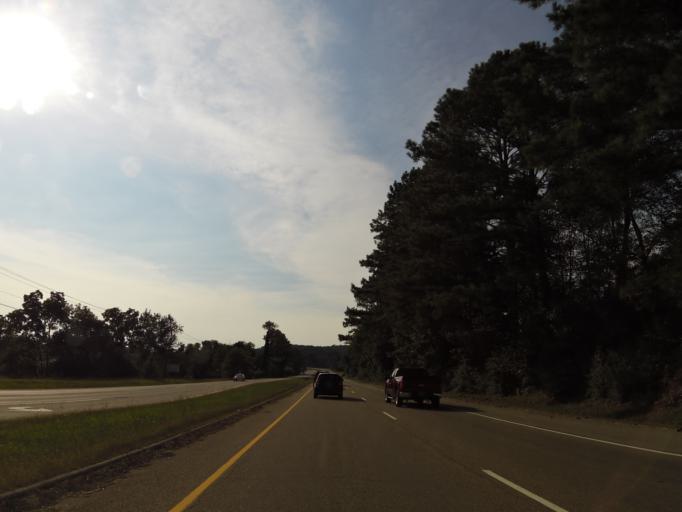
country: US
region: Tennessee
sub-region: Loudon County
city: Lenoir City
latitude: 35.8370
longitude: -84.2925
